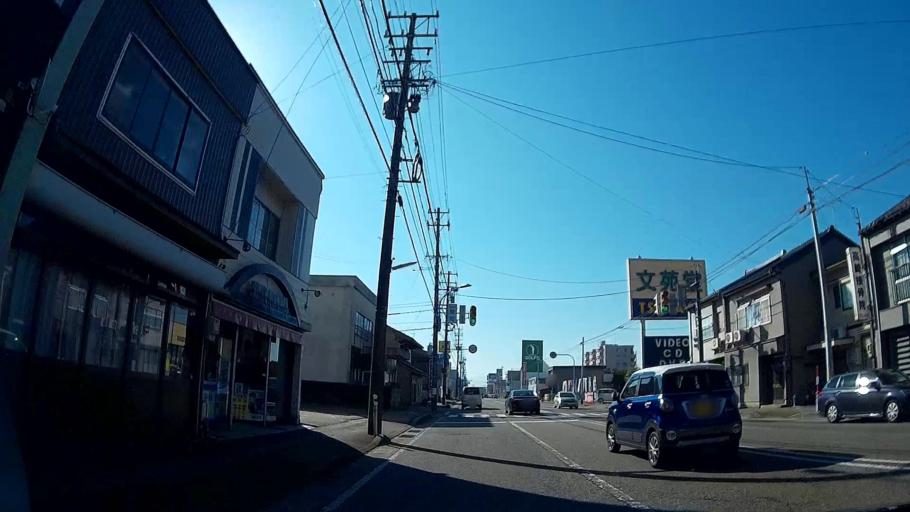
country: JP
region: Toyama
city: Takaoka
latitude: 36.7374
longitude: 137.0035
